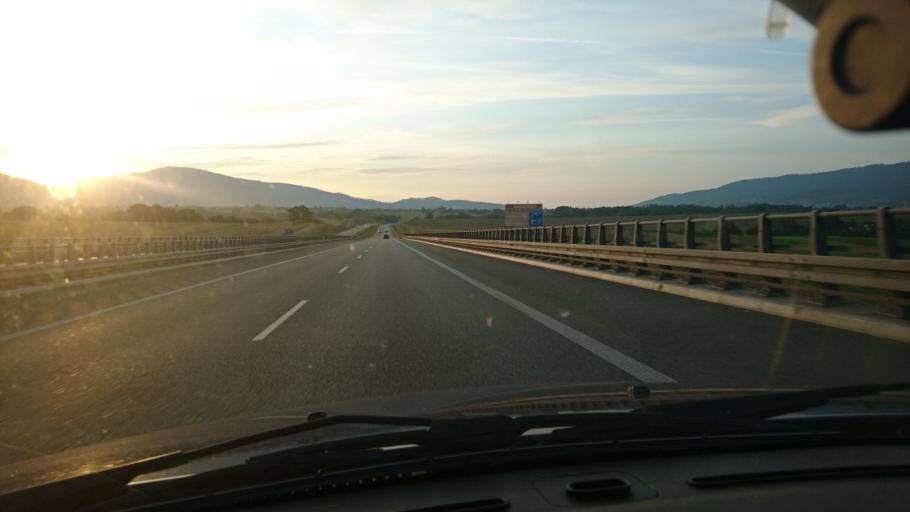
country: PL
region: Silesian Voivodeship
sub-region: Powiat zywiecki
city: Lesna
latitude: 49.6989
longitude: 19.1311
